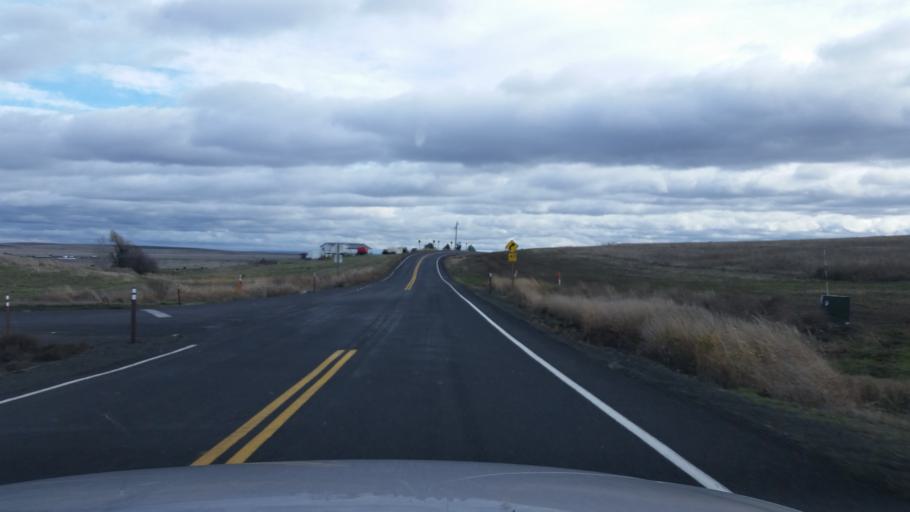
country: US
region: Washington
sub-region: Lincoln County
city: Davenport
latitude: 47.3433
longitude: -118.0074
